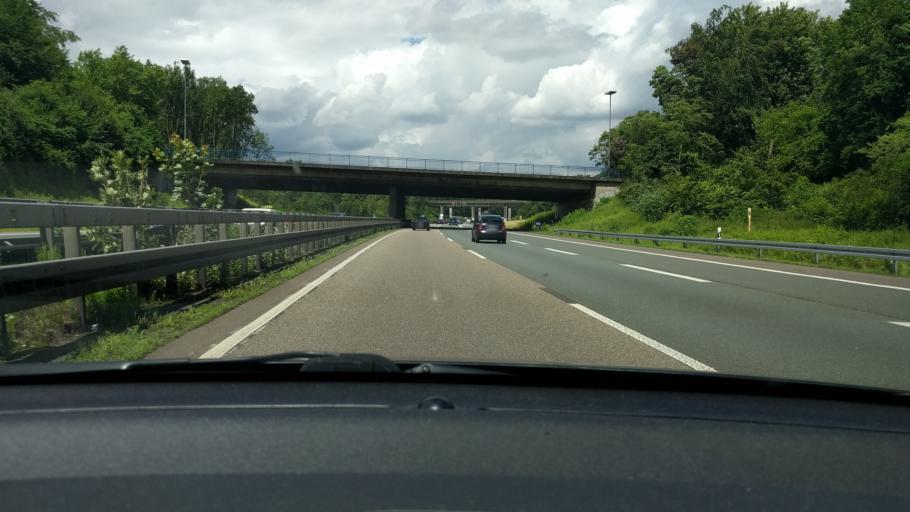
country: DE
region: North Rhine-Westphalia
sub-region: Regierungsbezirk Arnsberg
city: Bochum
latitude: 51.4775
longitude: 7.2805
